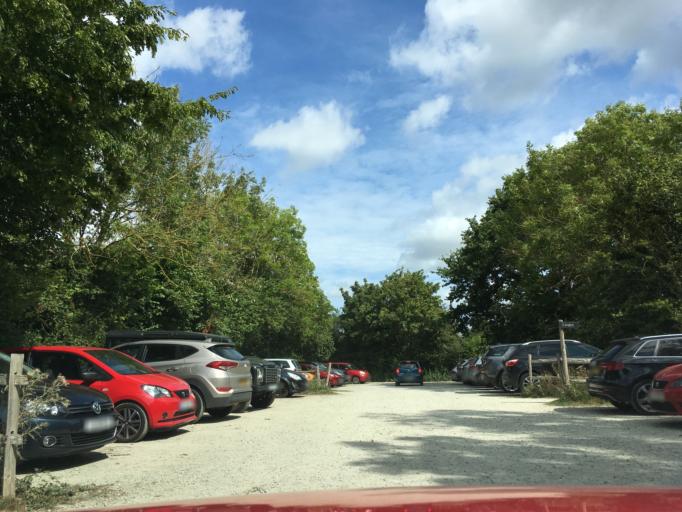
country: GB
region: England
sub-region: Kent
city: Cranbrook
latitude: 51.1164
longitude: 0.5776
